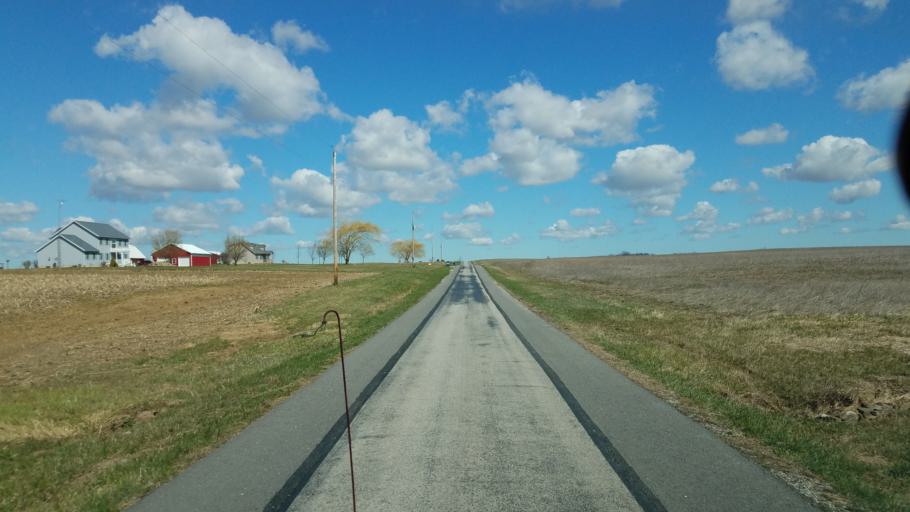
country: US
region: Ohio
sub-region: Sandusky County
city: Mount Carmel
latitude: 41.0858
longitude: -82.9383
